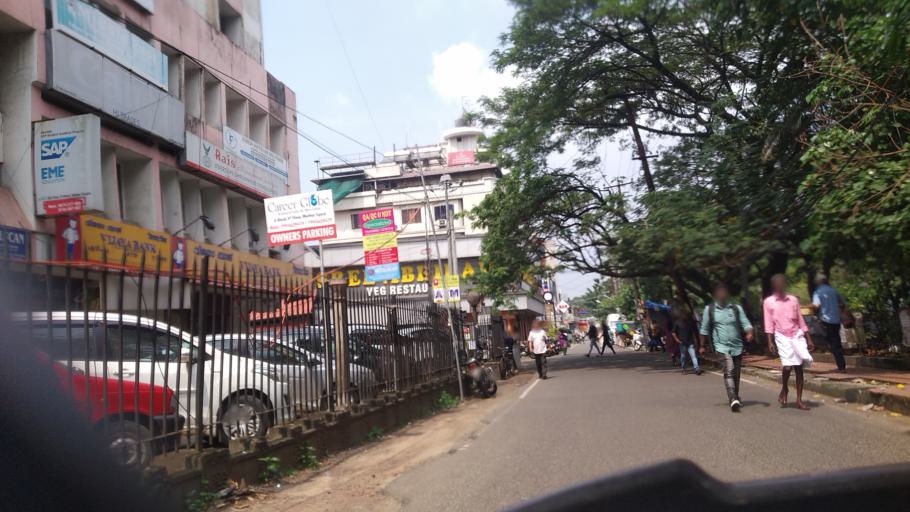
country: IN
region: Kerala
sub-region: Ernakulam
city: Cochin
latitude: 9.9911
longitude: 76.2862
